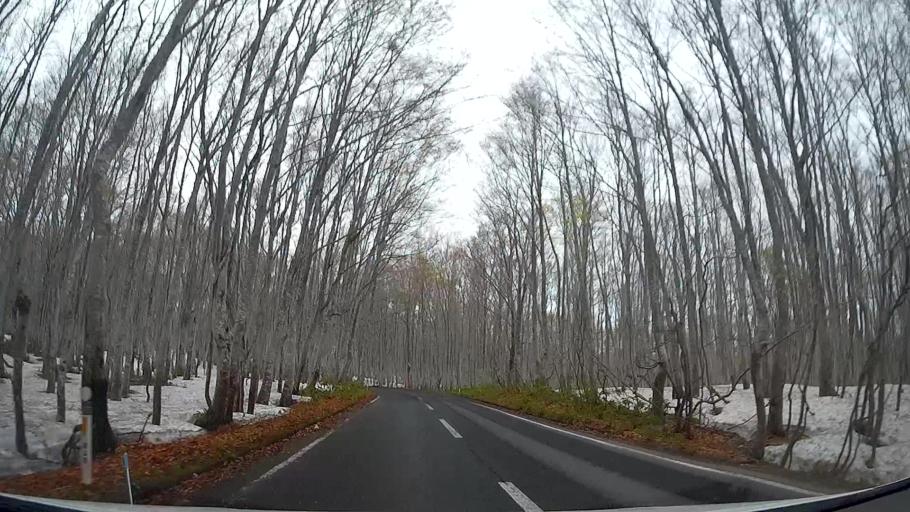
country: JP
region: Aomori
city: Aomori Shi
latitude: 40.6305
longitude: 140.9343
